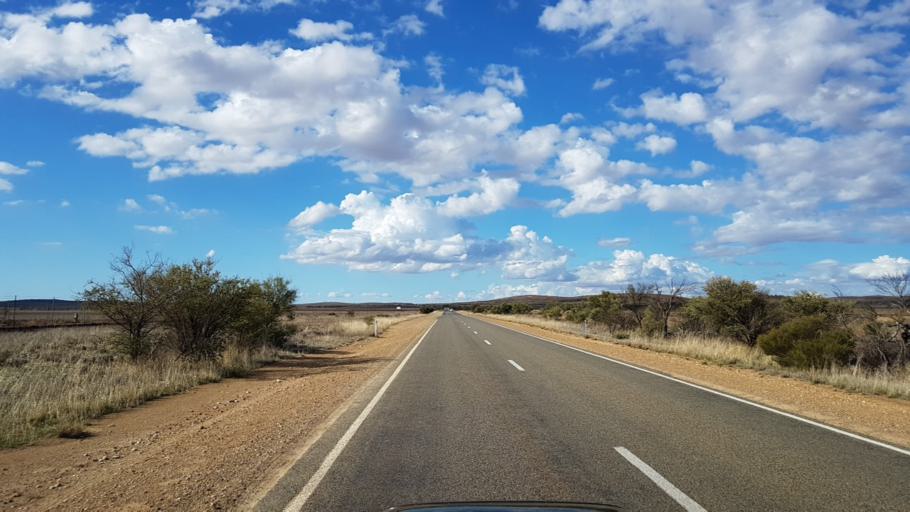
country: AU
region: South Australia
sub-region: Peterborough
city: Peterborough
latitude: -32.9680
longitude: 138.8703
